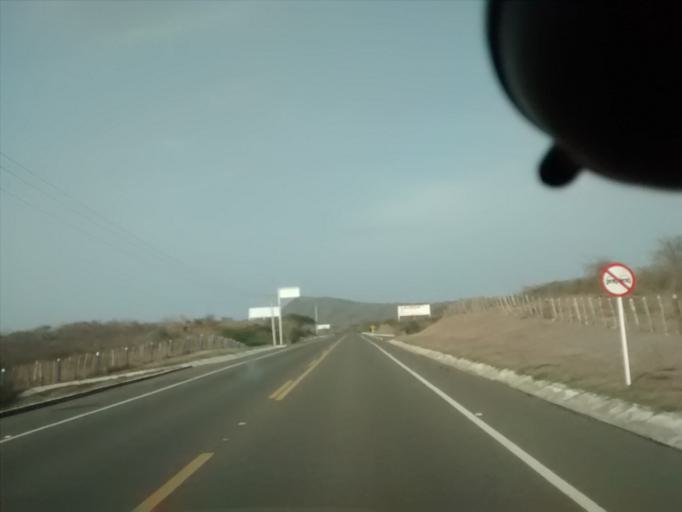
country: CO
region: Atlantico
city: Juan de Acosta
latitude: 10.8644
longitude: -75.0990
